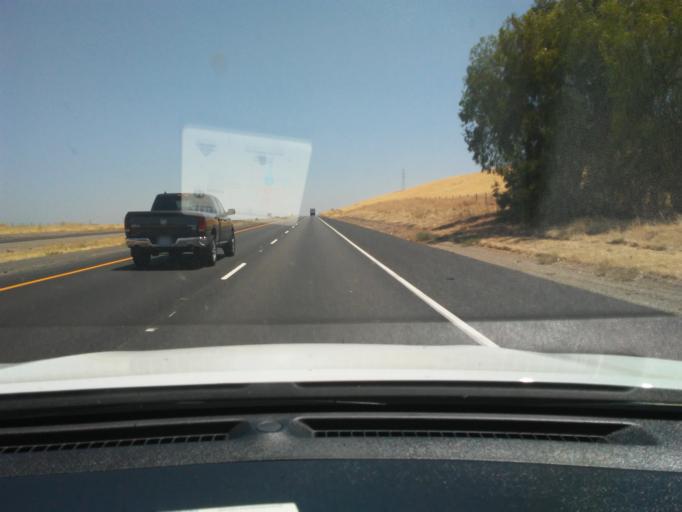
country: US
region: California
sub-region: San Joaquin County
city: Tracy
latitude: 37.6294
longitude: -121.3869
